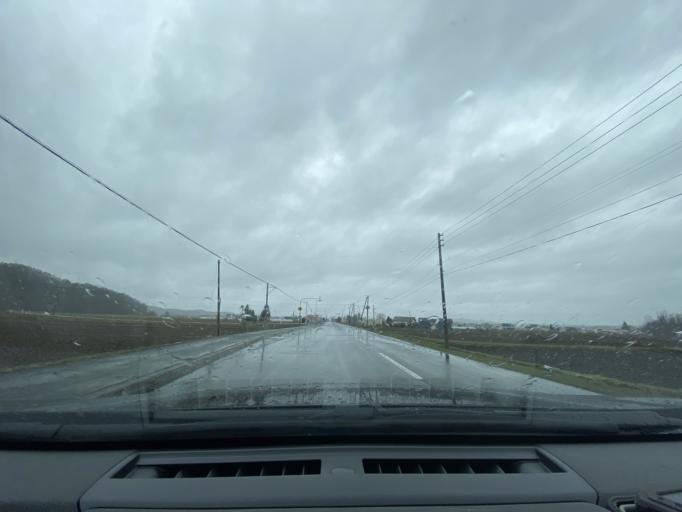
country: JP
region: Hokkaido
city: Fukagawa
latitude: 43.8082
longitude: 142.0353
